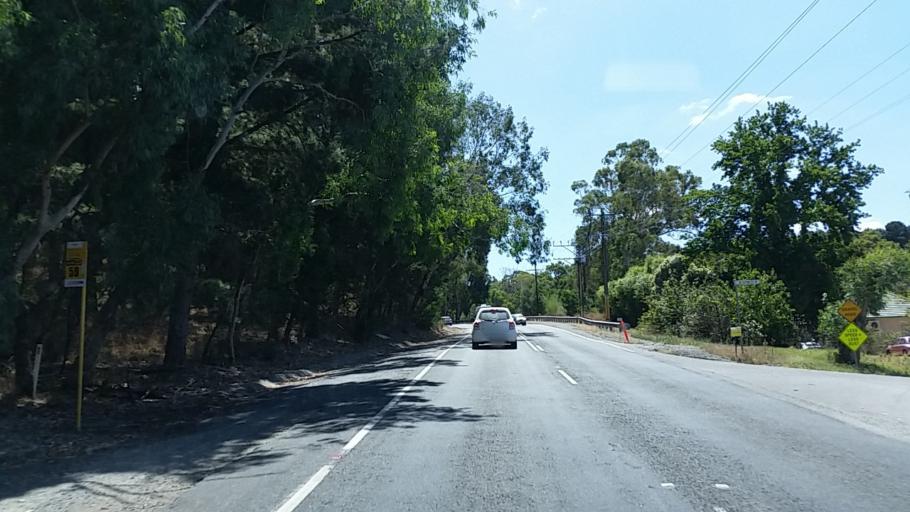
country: AU
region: South Australia
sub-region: Mount Barker
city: Little Hampton
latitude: -35.0490
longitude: 138.8391
